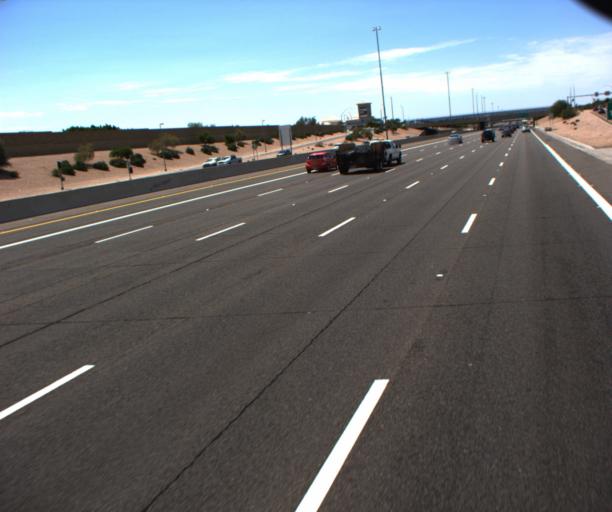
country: US
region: Arizona
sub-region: Maricopa County
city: Gilbert
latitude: 33.3867
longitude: -111.7499
